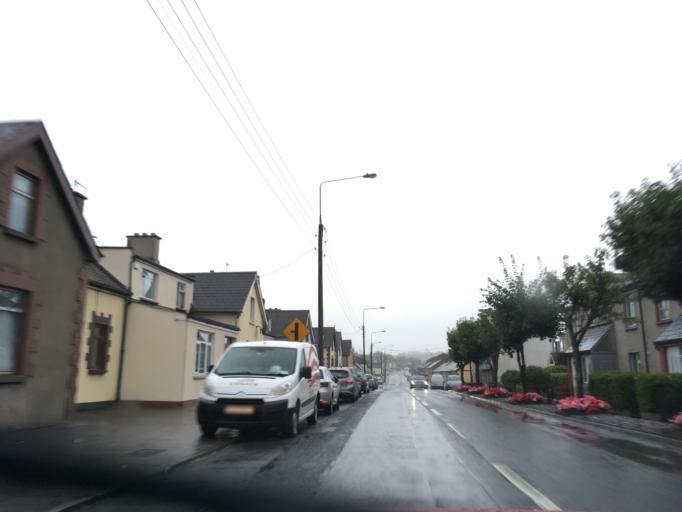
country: IE
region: Munster
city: Tipperary
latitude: 52.4748
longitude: -8.1542
